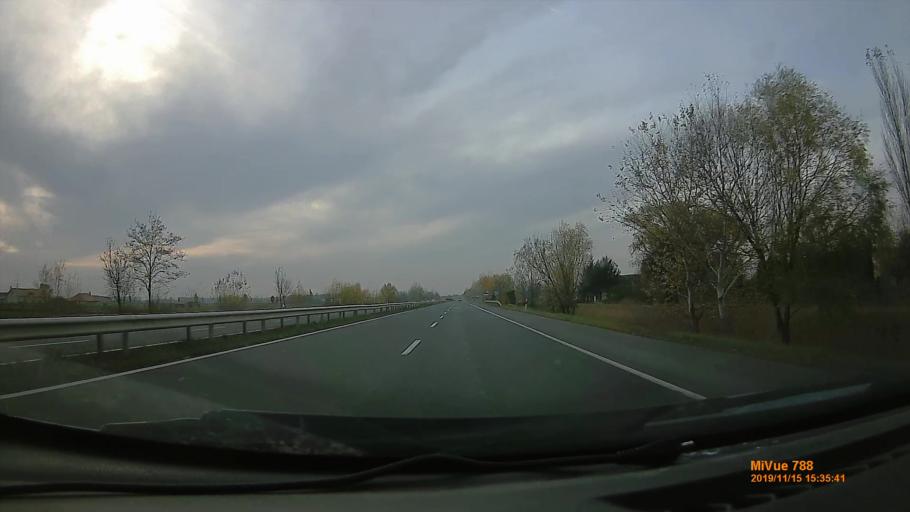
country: HU
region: Bekes
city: Gyula
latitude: 46.6553
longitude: 21.2250
